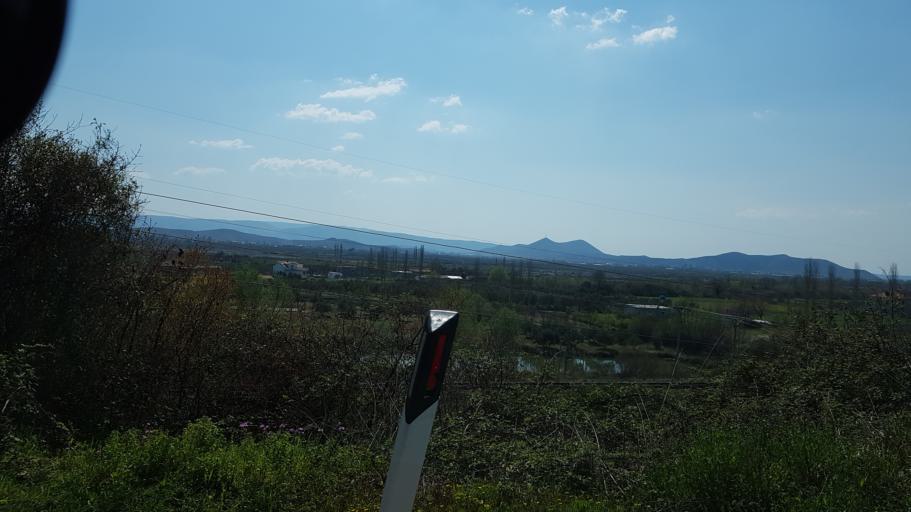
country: AL
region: Shkoder
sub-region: Rrethi i Shkodres
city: Vau i Dejes
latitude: 42.0105
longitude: 19.5915
